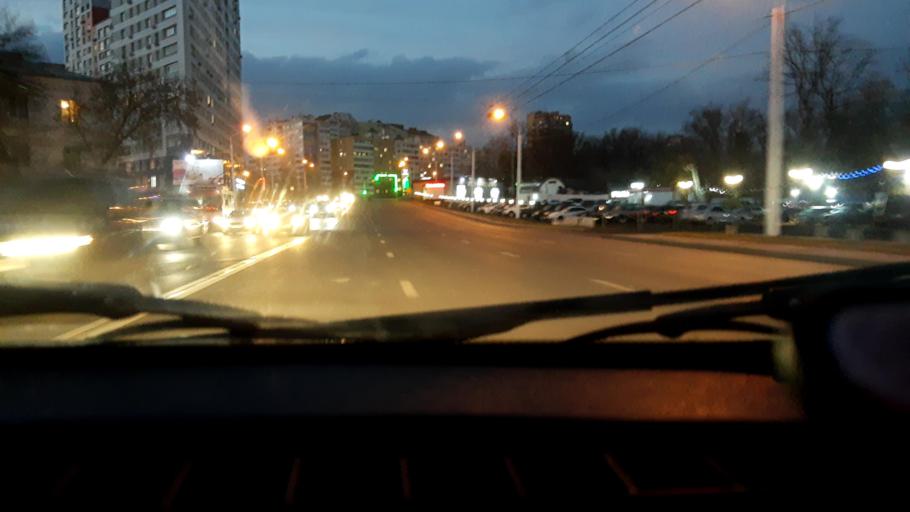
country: RU
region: Bashkortostan
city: Ufa
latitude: 54.7600
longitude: 56.0236
